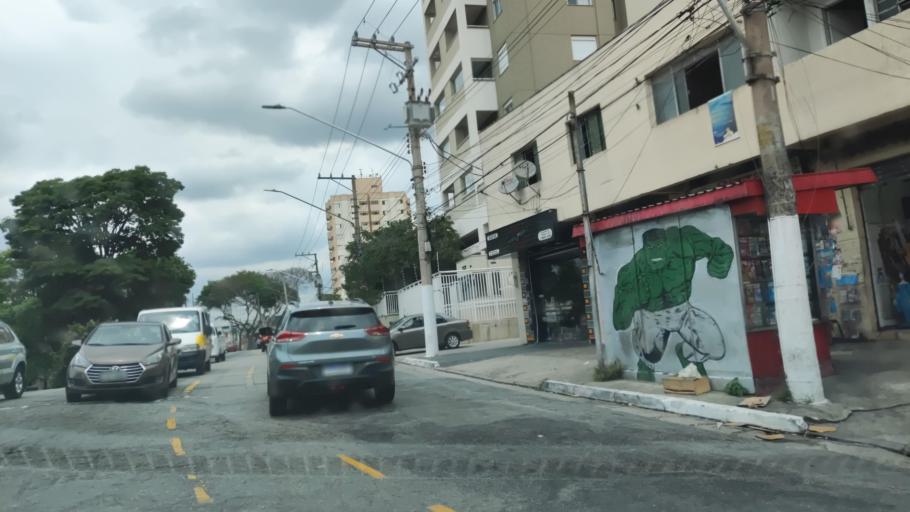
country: BR
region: Sao Paulo
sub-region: Sao Paulo
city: Sao Paulo
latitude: -23.4699
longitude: -46.6546
